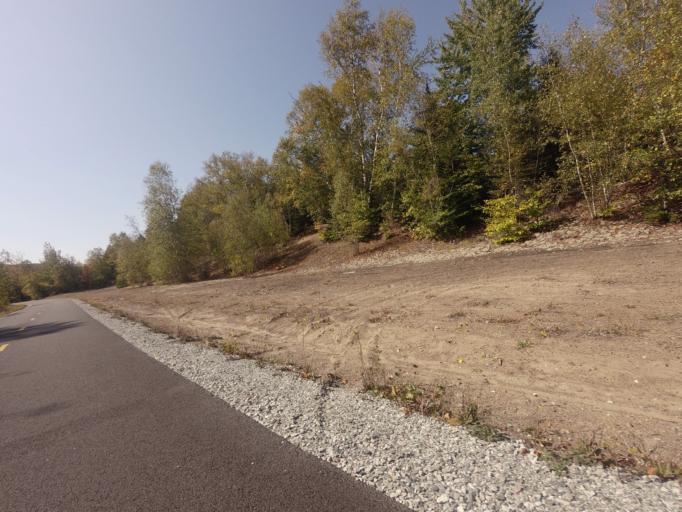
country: CA
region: Quebec
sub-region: Laurentides
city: Mont-Tremblant
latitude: 46.1333
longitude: -74.4911
